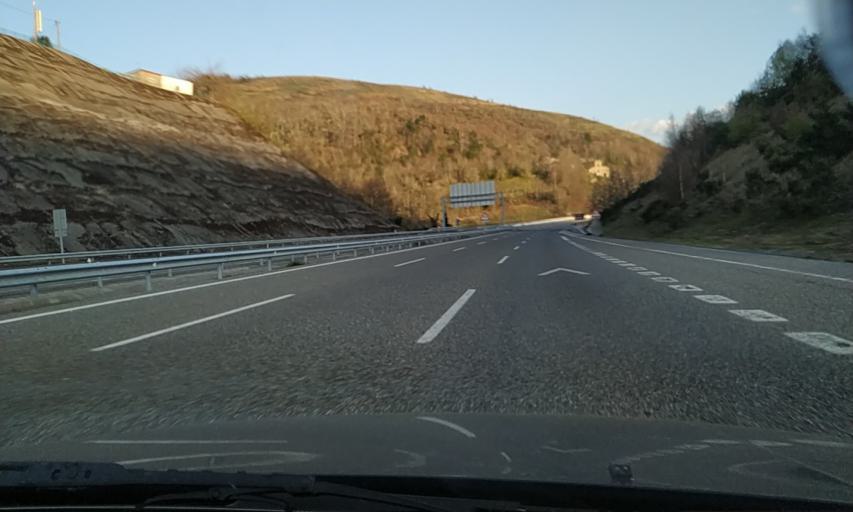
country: ES
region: Galicia
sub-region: Provincia de Lugo
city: San Roman
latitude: 42.7635
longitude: -7.0816
